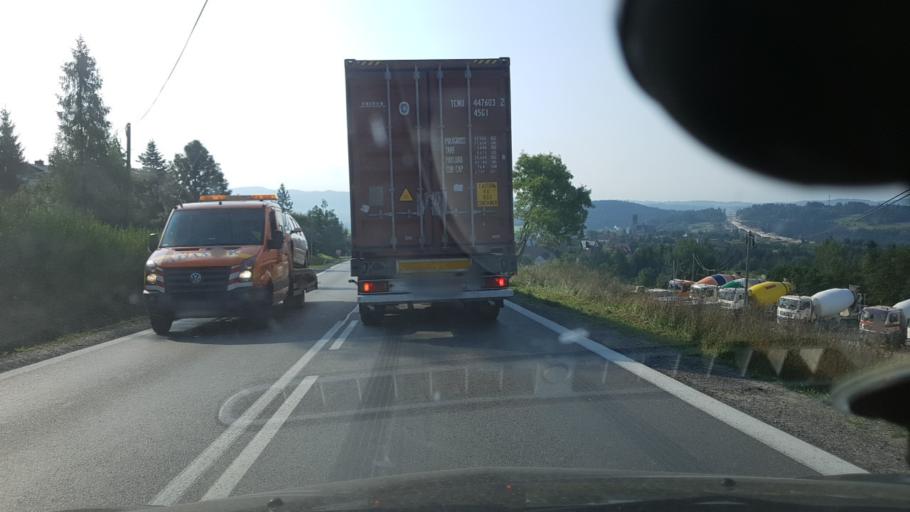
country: PL
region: Lesser Poland Voivodeship
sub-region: Powiat suski
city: Naprawa
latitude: 49.6513
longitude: 19.9083
